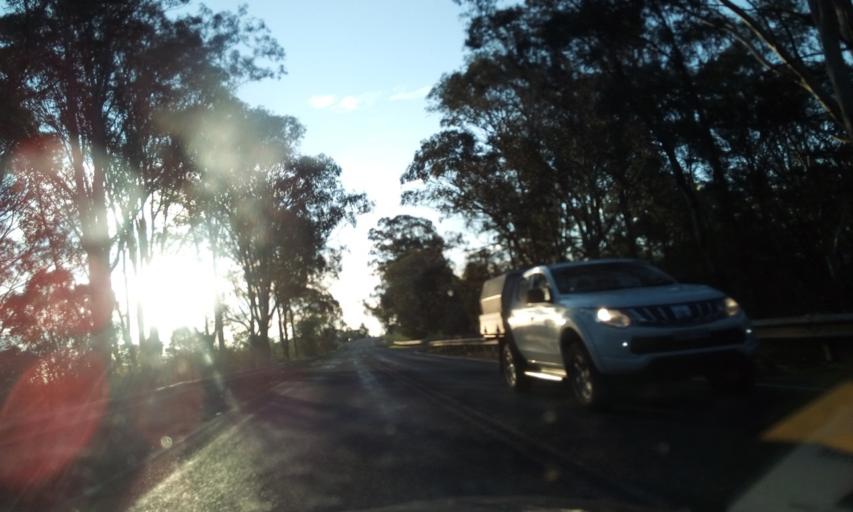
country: AU
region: New South Wales
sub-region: Wollondilly
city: Douglas Park
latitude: -34.2405
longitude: 150.7032
